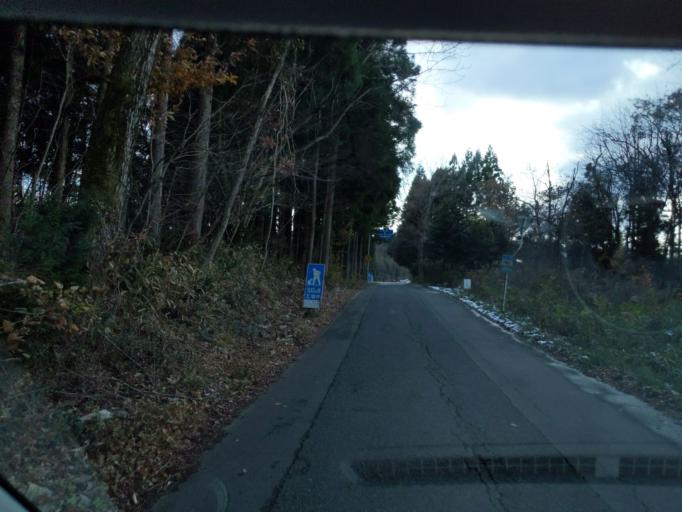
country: JP
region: Iwate
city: Mizusawa
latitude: 39.1150
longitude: 141.0824
